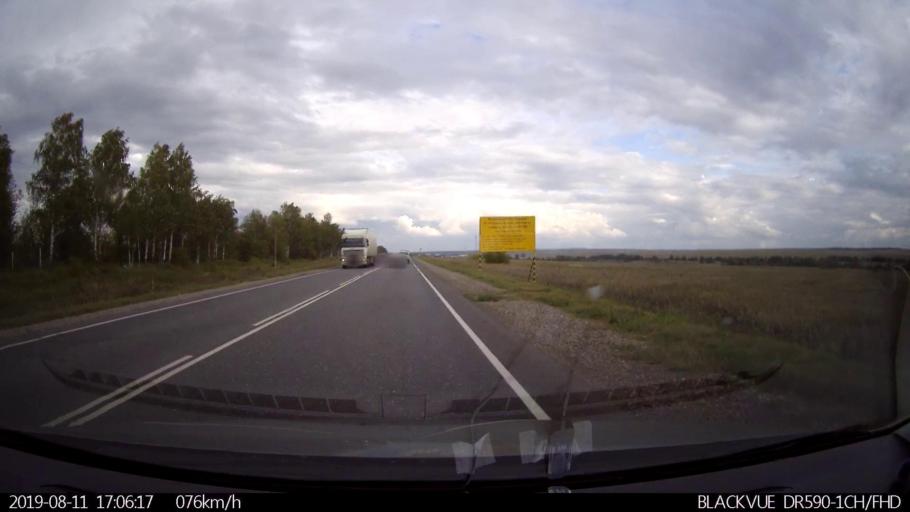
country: RU
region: Ulyanovsk
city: Mayna
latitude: 54.2951
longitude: 47.8030
